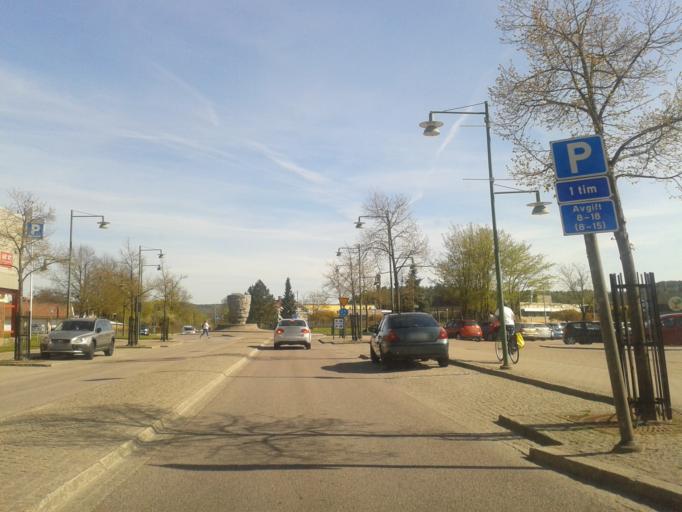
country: SE
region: Vaestra Goetaland
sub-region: Kungalvs Kommun
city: Kungalv
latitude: 57.8691
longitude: 11.9825
